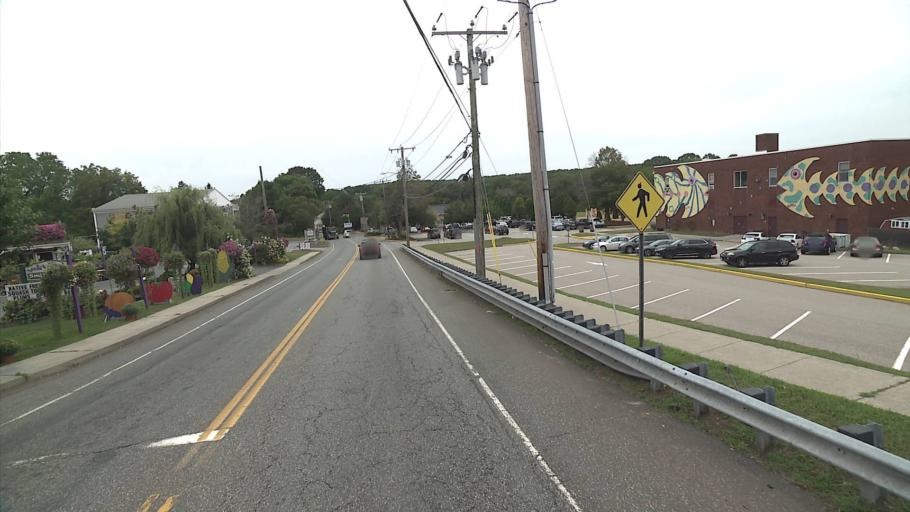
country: US
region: Connecticut
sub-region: New London County
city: Niantic
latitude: 41.3222
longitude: -72.2029
